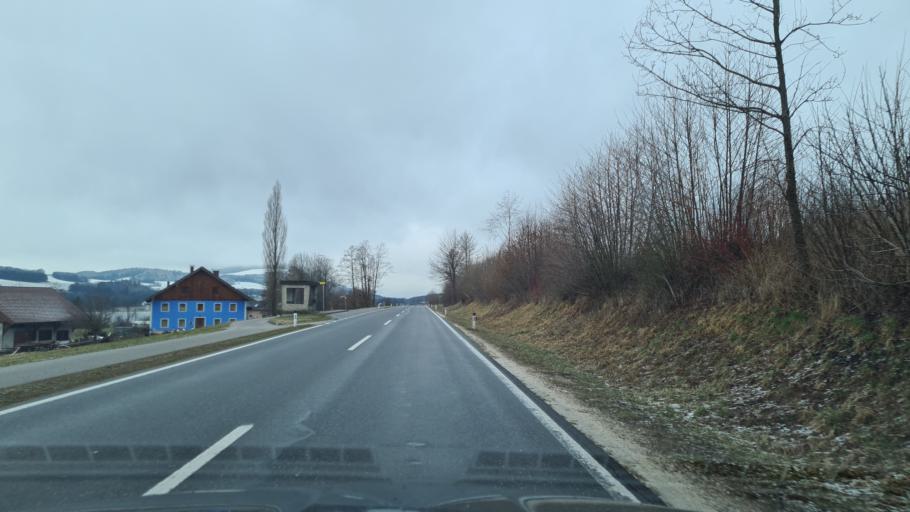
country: AT
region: Upper Austria
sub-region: Politischer Bezirk Vocklabruck
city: Zell am Moos
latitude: 47.9206
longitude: 13.3163
